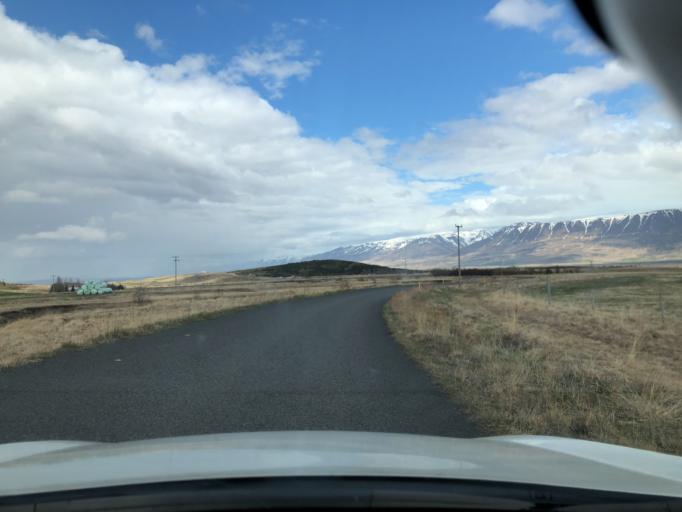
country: IS
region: Northwest
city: Saudarkrokur
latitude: 65.5396
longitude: -19.4713
